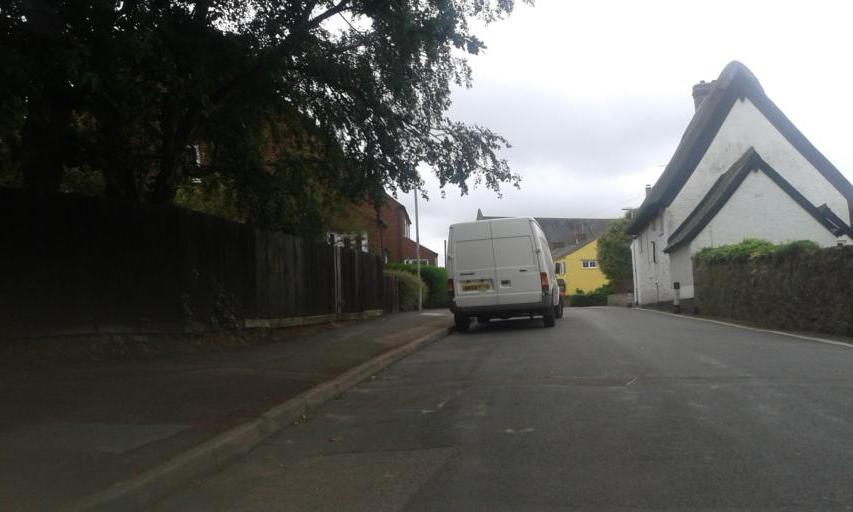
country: GB
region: England
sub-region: Leicestershire
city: Enderby
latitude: 52.5904
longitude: -1.2145
